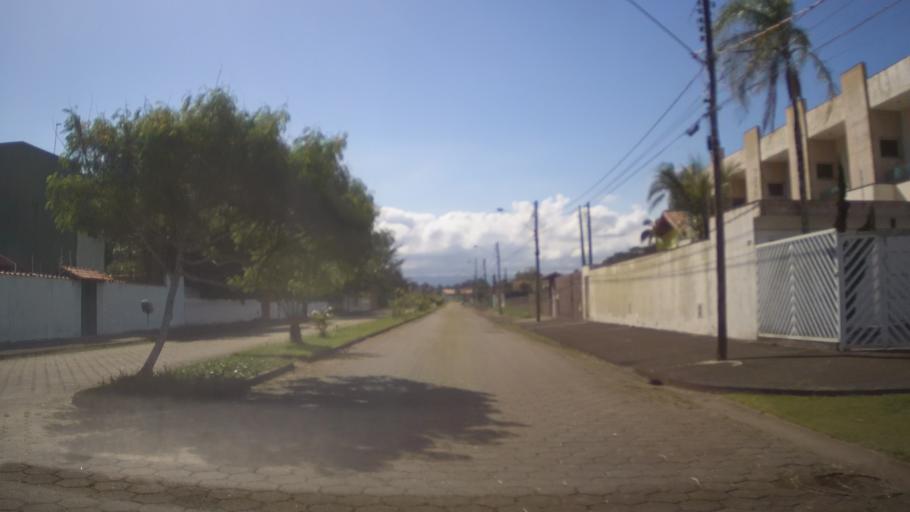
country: BR
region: Sao Paulo
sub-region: Itanhaem
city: Itanhaem
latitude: -24.2216
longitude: -46.8572
